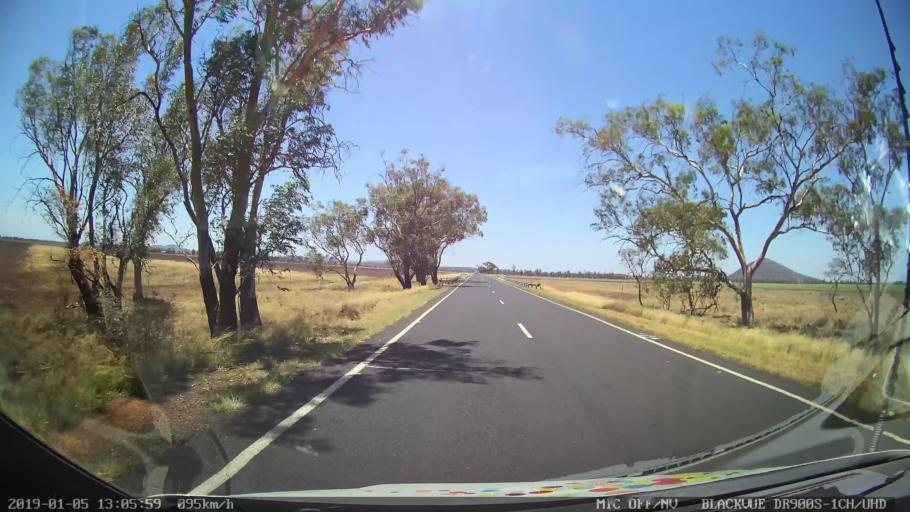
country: AU
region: New South Wales
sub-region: Gunnedah
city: Gunnedah
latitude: -31.0952
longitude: 149.8611
